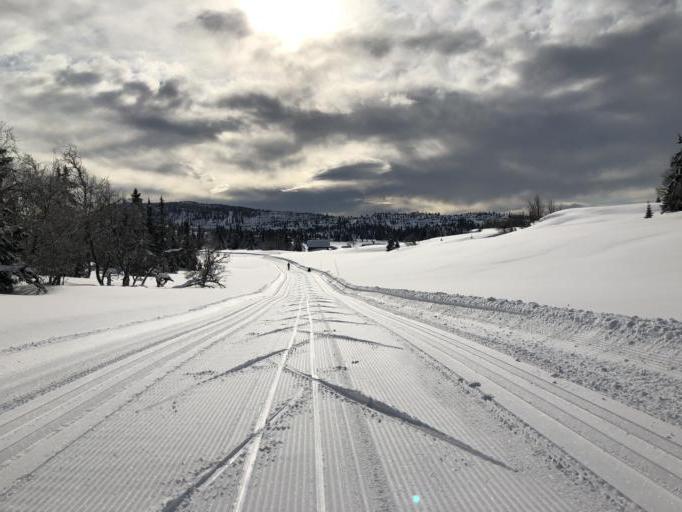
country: NO
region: Oppland
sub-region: Gausdal
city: Segalstad bru
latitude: 61.3180
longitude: 10.0591
